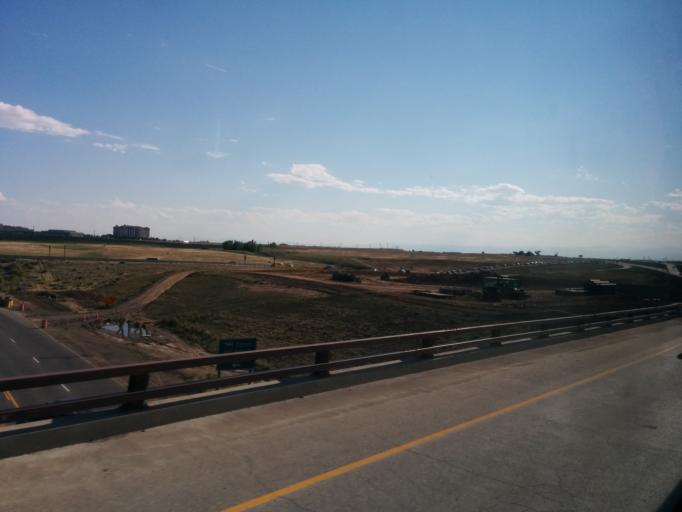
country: US
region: Colorado
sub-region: Adams County
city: Aurora
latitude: 39.8335
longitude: -104.7718
